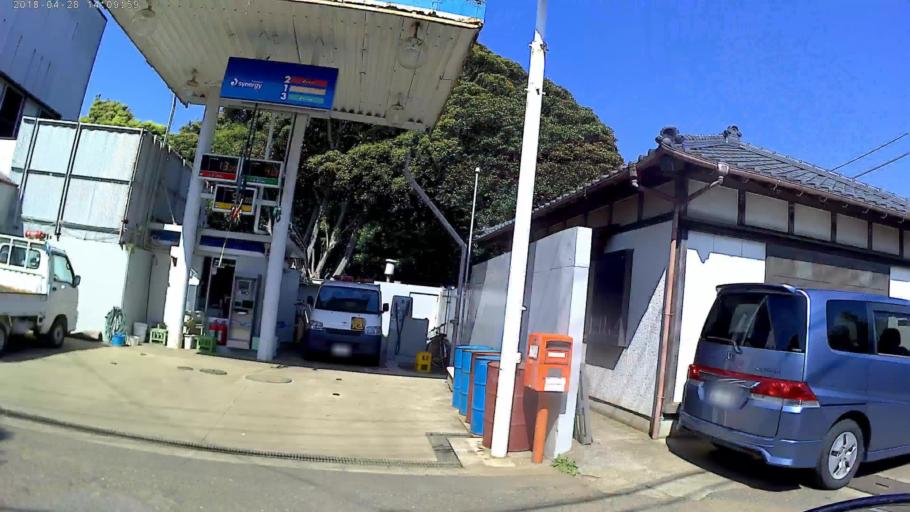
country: JP
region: Kanagawa
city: Miura
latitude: 35.1450
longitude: 139.6531
